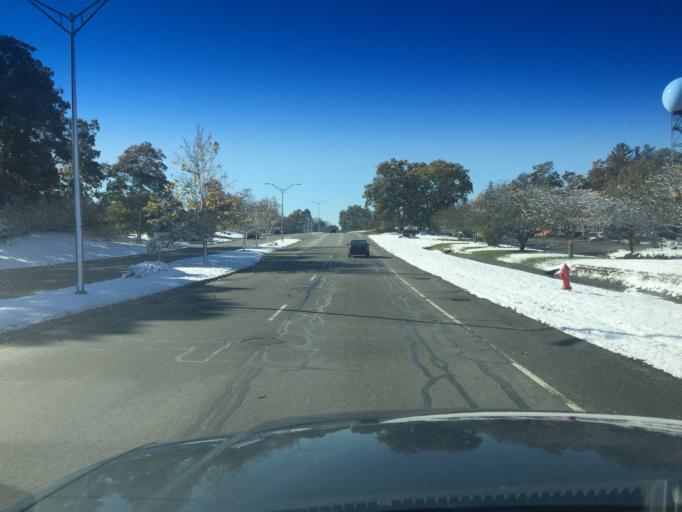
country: US
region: Massachusetts
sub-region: Bristol County
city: Norton Center
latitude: 41.9568
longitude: -71.1347
